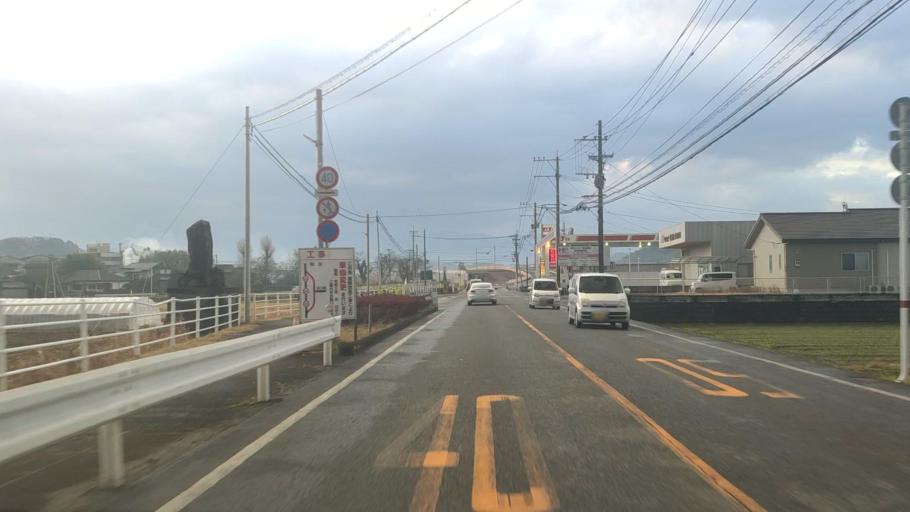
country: JP
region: Kumamoto
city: Uto
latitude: 32.7043
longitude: 130.7781
